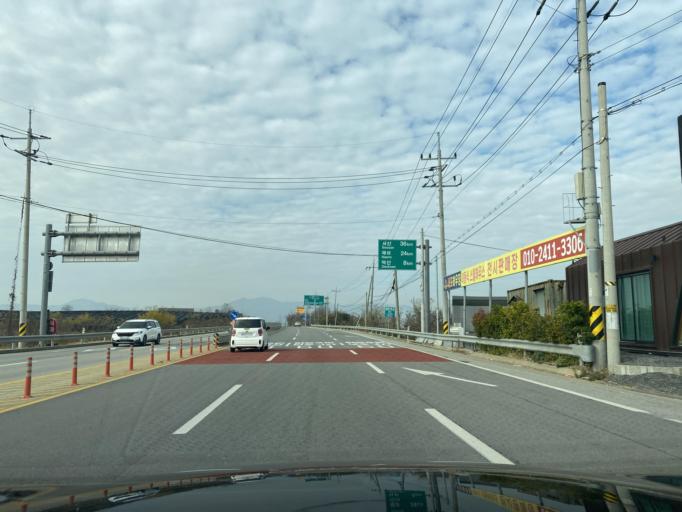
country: KR
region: Chungcheongnam-do
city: Yesan
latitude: 36.6899
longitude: 126.7502
